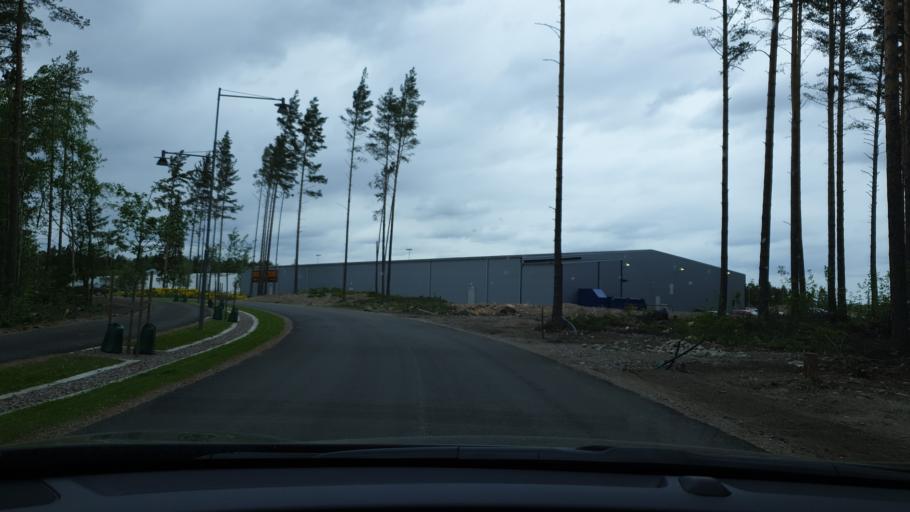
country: SE
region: Gaevleborg
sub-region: Gavle Kommun
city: Gavle
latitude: 60.6432
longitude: 17.1487
